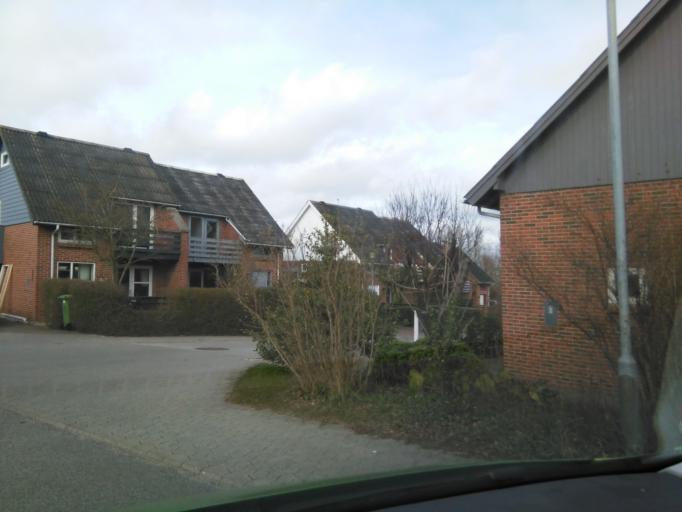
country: DK
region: Central Jutland
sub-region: Arhus Kommune
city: Arhus
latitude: 56.1902
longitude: 10.1974
